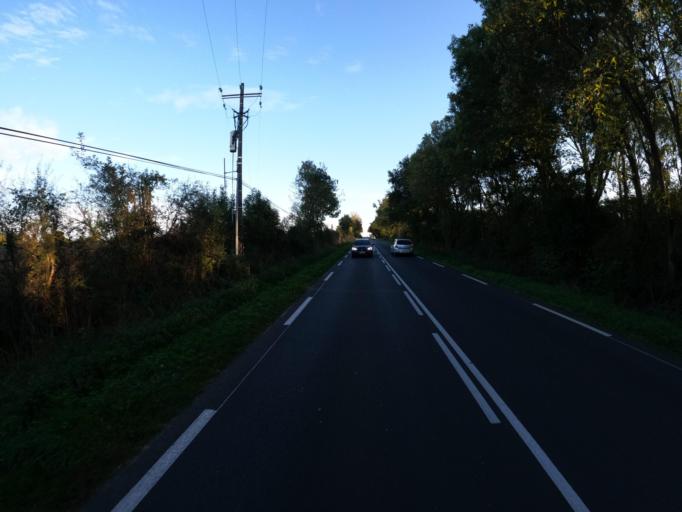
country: FR
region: Pays de la Loire
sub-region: Departement de la Vendee
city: Bournezeau
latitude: 46.6246
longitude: -1.1585
